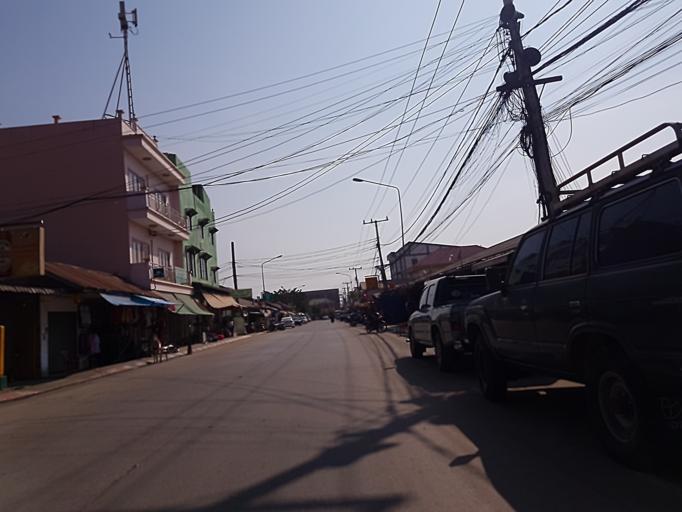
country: LA
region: Vientiane
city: Vientiane
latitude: 17.9486
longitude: 102.6399
